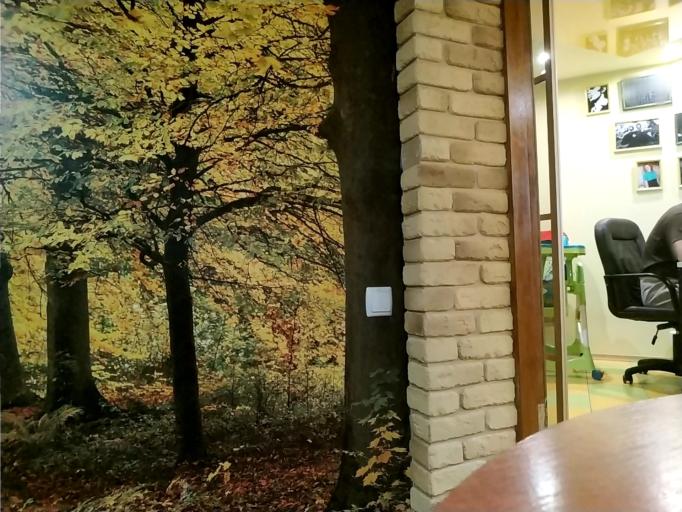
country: RU
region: Tverskaya
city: Staraya Toropa
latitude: 56.3385
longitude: 31.8598
